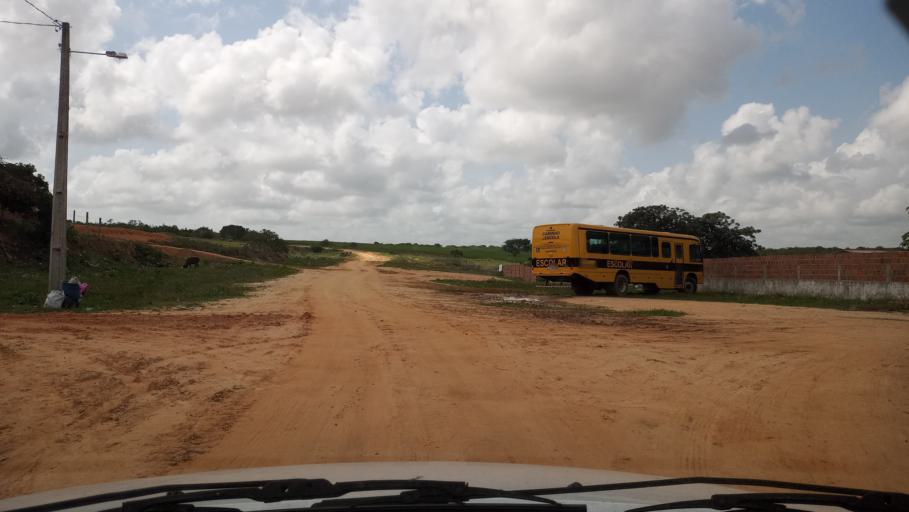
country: BR
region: Rio Grande do Norte
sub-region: Ares
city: Ares
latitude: -6.2349
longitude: -35.1294
